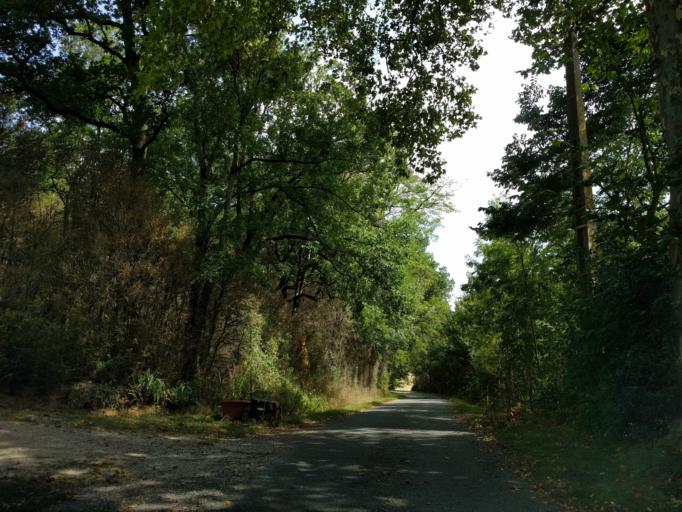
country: FR
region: Midi-Pyrenees
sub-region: Departement du Tarn
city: Saix
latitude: 43.6429
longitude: 2.1901
